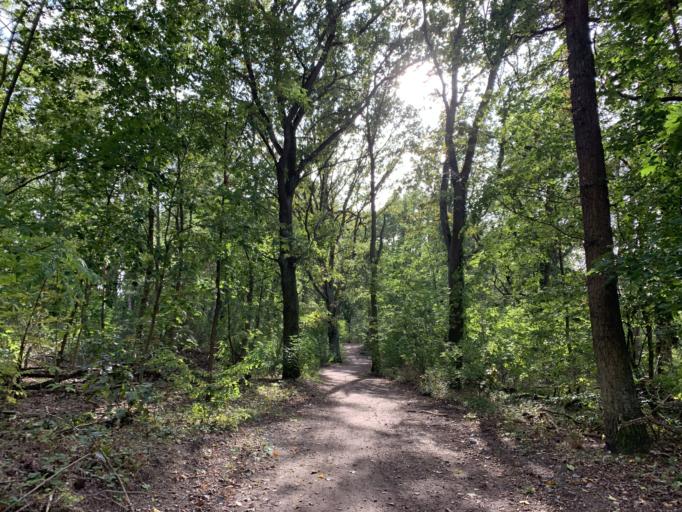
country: DE
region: Berlin
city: Wannsee
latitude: 52.4108
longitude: 13.1547
